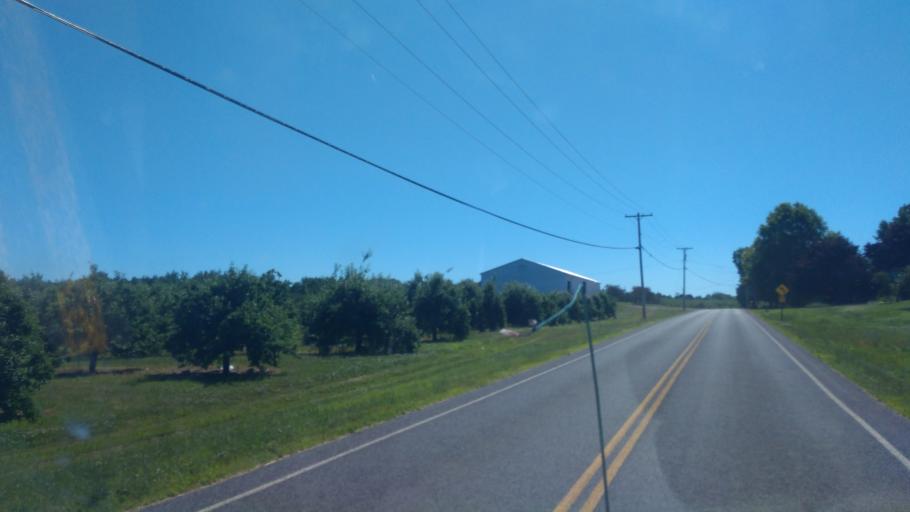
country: US
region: New York
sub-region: Wayne County
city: Sodus
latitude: 43.2742
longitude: -77.1099
